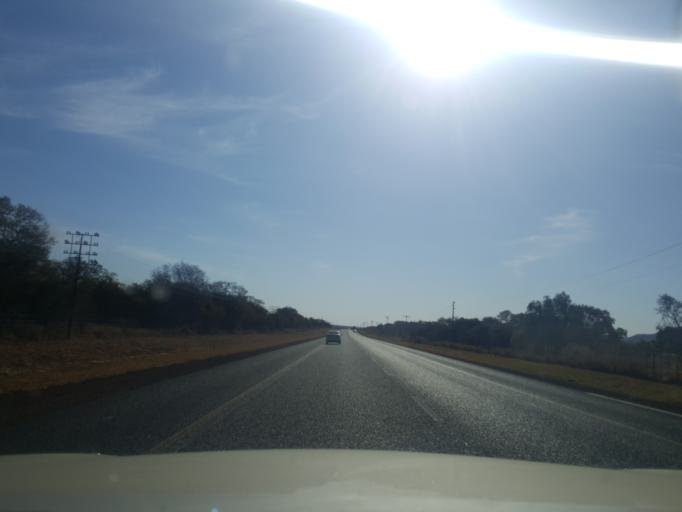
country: ZA
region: North-West
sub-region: Ngaka Modiri Molema District Municipality
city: Zeerust
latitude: -25.5246
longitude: 26.1841
